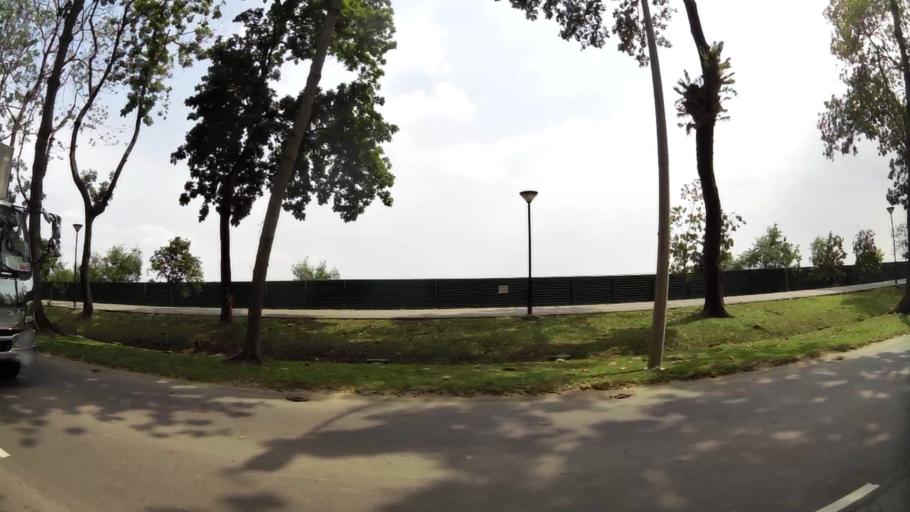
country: SG
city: Singapore
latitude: 1.3434
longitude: 103.9941
